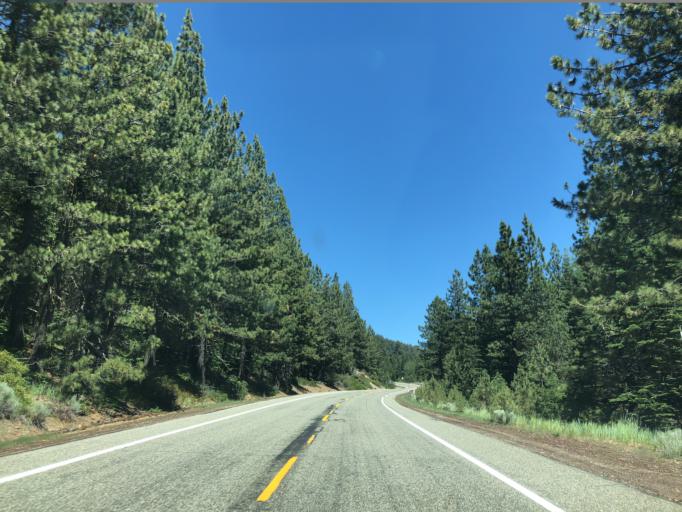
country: US
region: California
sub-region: Shasta County
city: Shingletown
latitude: 40.5414
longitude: -121.5842
